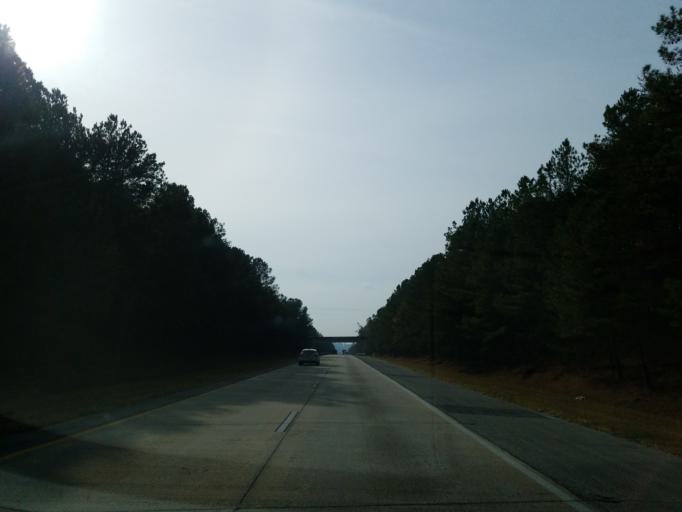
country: US
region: Georgia
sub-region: Cherokee County
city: Ball Ground
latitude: 34.3619
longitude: -84.3917
